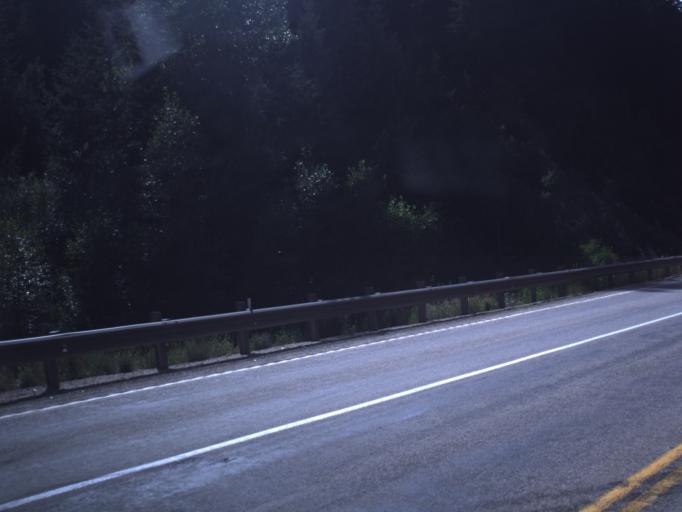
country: US
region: Utah
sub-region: Wasatch County
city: Heber
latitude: 40.3552
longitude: -111.2793
